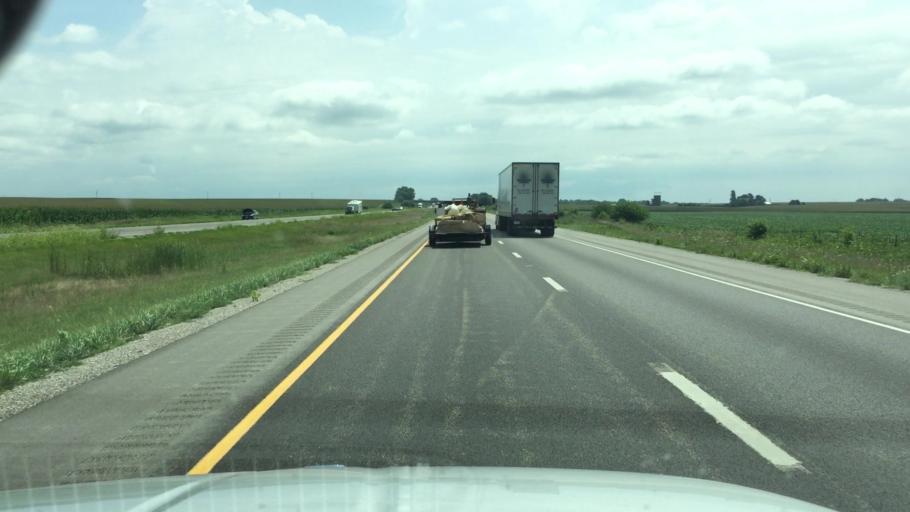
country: US
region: Illinois
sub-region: Peoria County
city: Elmwood
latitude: 40.8725
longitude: -90.0544
